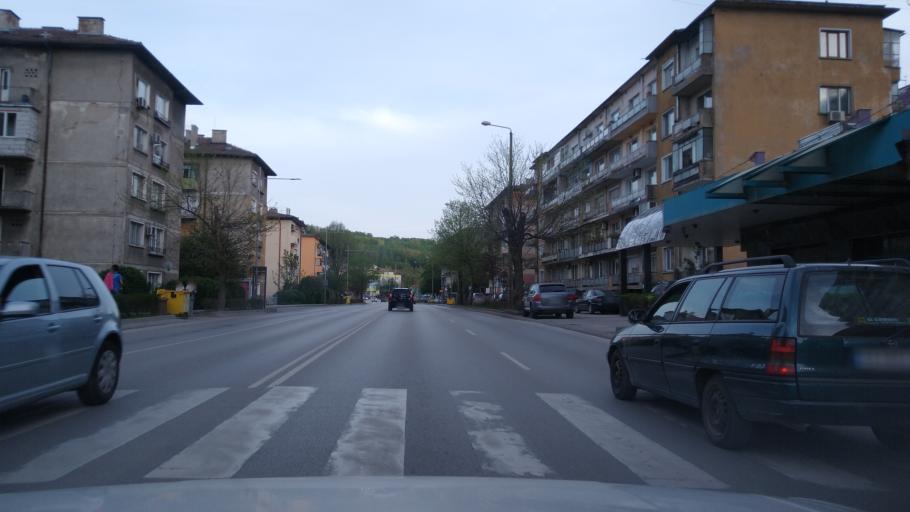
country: BG
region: Gabrovo
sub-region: Obshtina Gabrovo
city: Gabrovo
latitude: 42.8636
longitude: 25.3193
